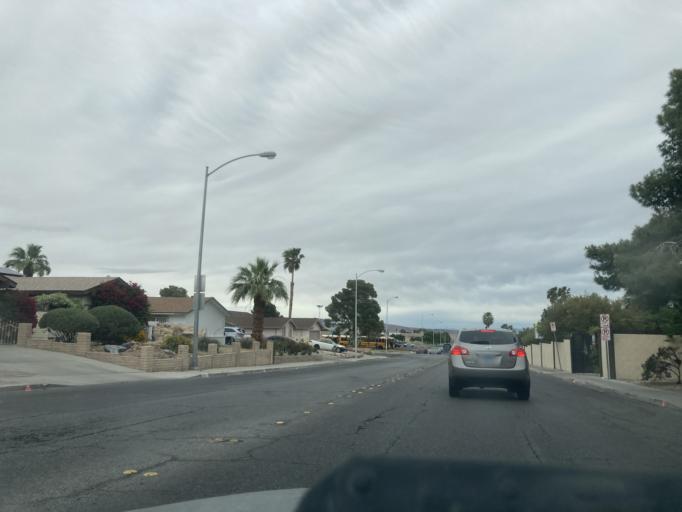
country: US
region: Nevada
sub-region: Clark County
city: Winchester
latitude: 36.1187
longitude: -115.0895
